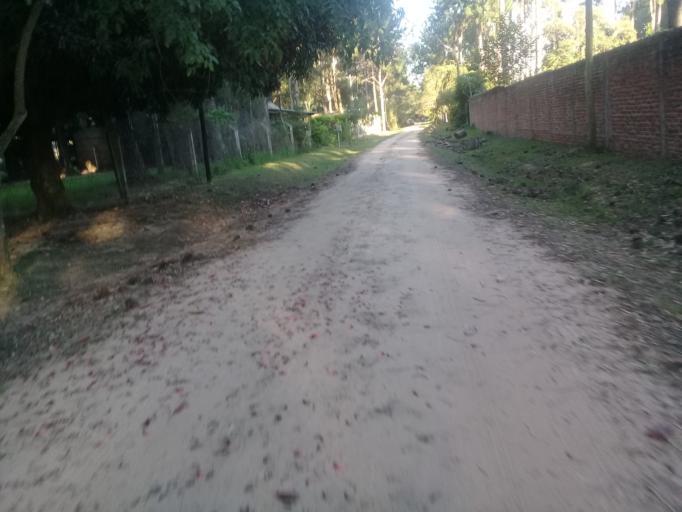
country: AR
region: Corrientes
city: San Luis del Palmar
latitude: -27.4638
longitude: -58.6659
